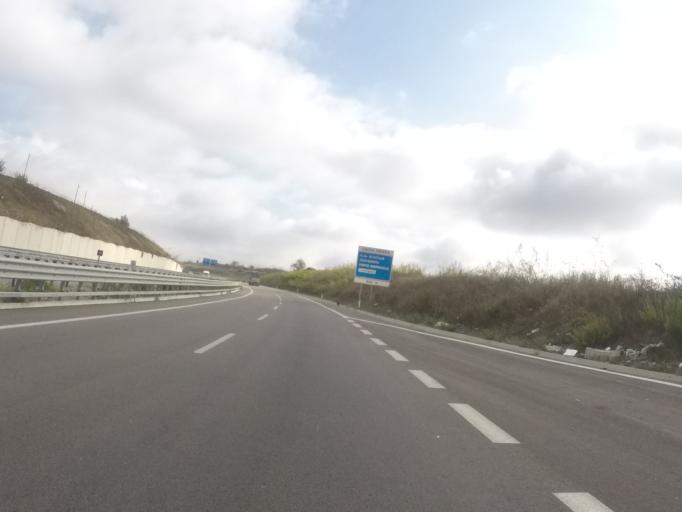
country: IT
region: Sicily
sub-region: Agrigento
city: Favara
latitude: 37.3497
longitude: 13.6759
